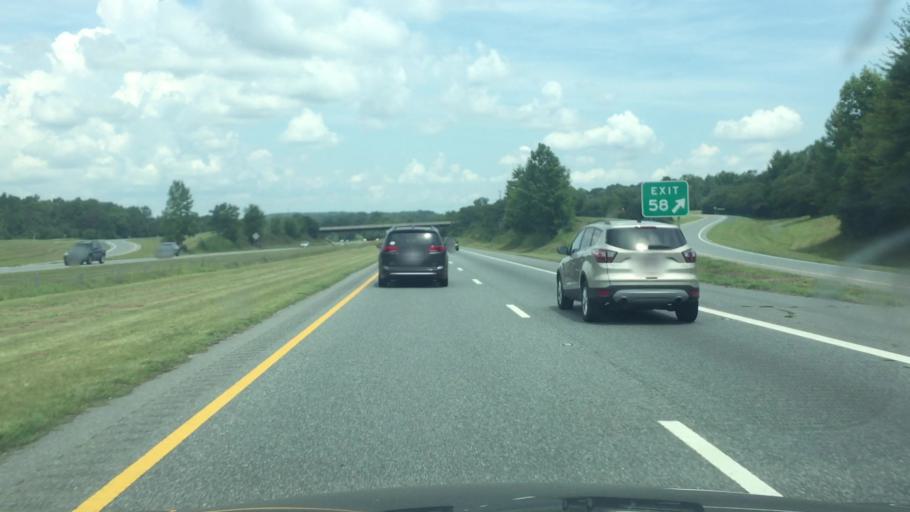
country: US
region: North Carolina
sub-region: Montgomery County
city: Biscoe
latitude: 35.4859
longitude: -79.7808
